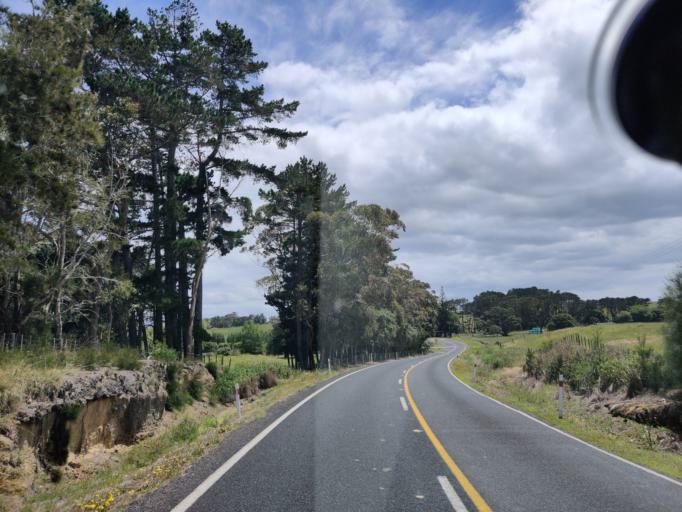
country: NZ
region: Northland
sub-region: Far North District
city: Kaitaia
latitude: -34.7106
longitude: 173.0351
